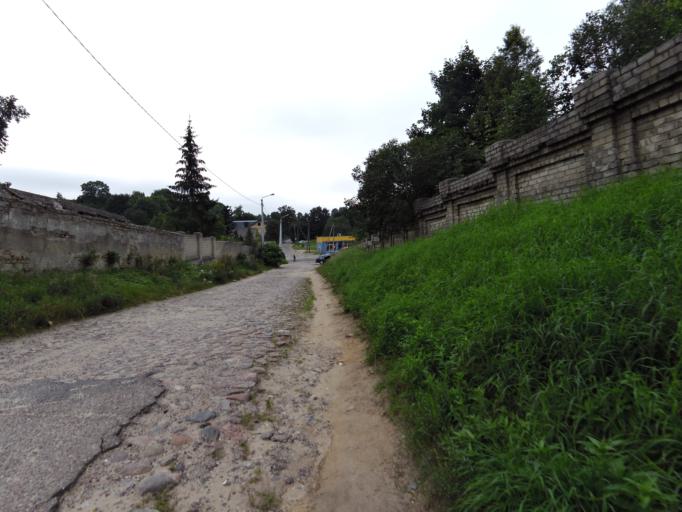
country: LT
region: Vilnius County
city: Rasos
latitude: 54.6652
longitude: 25.2932
